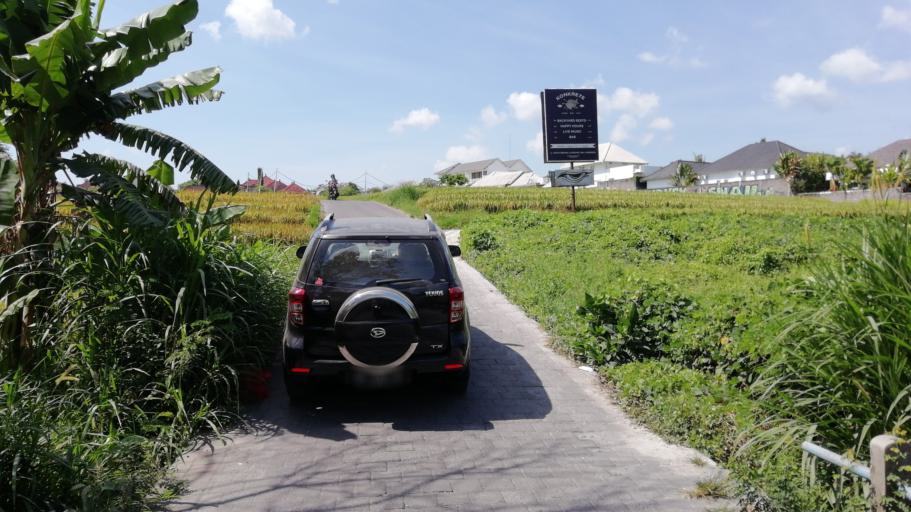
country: ID
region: Bali
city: Banjar Kerobokan
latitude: -8.6533
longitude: 115.1388
